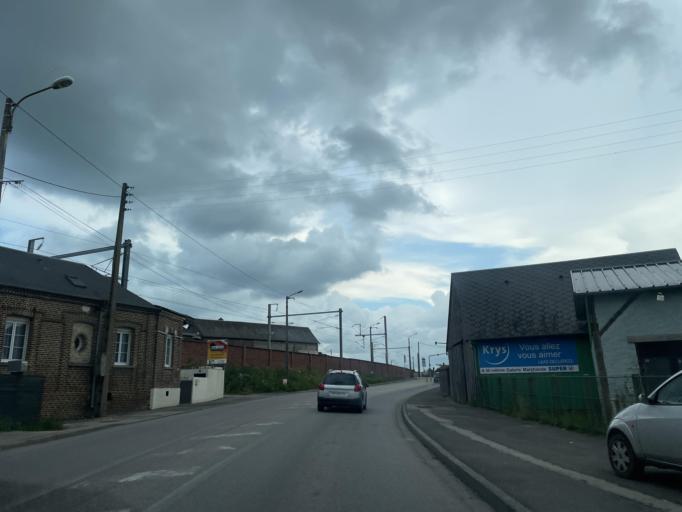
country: FR
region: Haute-Normandie
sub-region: Departement de la Seine-Maritime
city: Gournay-en-Bray
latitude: 49.4842
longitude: 1.7337
